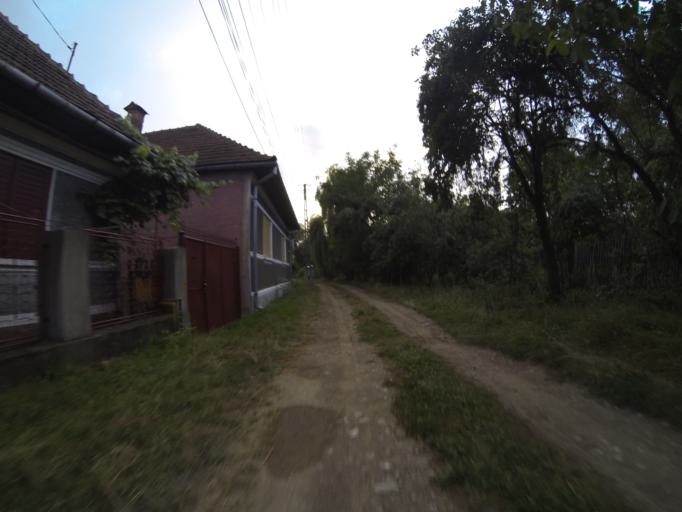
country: RO
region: Brasov
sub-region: Comuna Sinca Veche
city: Sinca Veche
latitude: 45.7638
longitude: 25.1708
